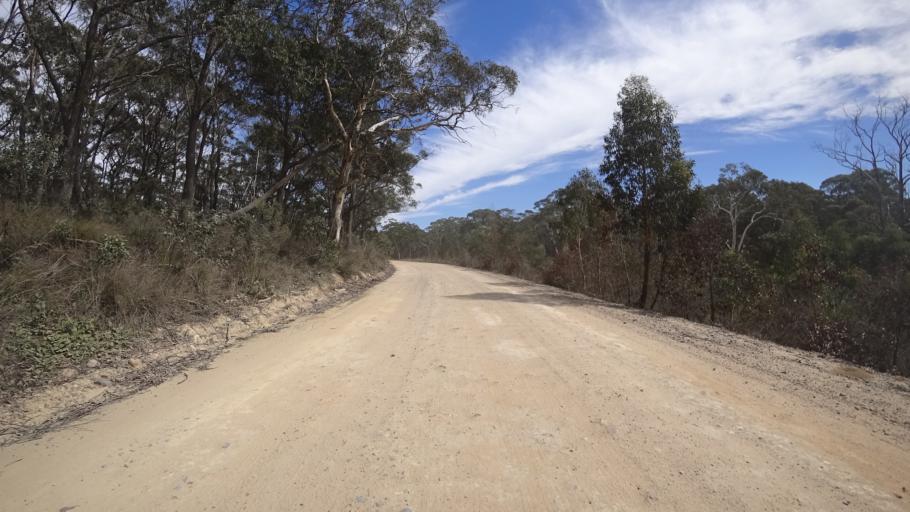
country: AU
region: New South Wales
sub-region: Lithgow
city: Lithgow
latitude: -33.3165
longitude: 150.2457
